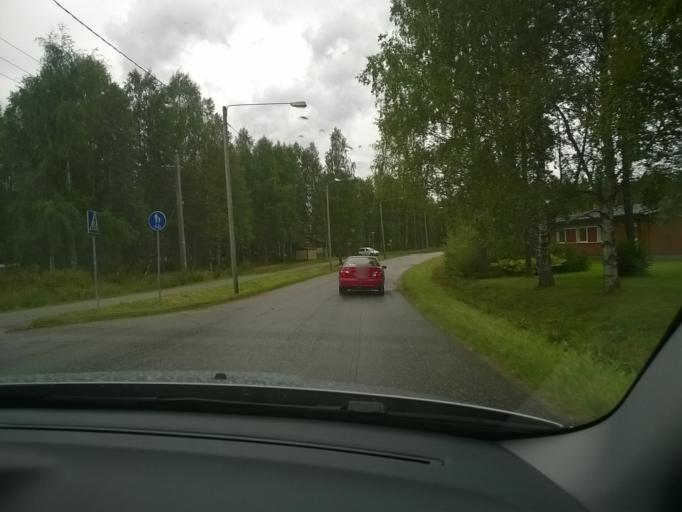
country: FI
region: Kainuu
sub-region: Kehys-Kainuu
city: Kuhmo
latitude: 64.1286
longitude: 29.4707
